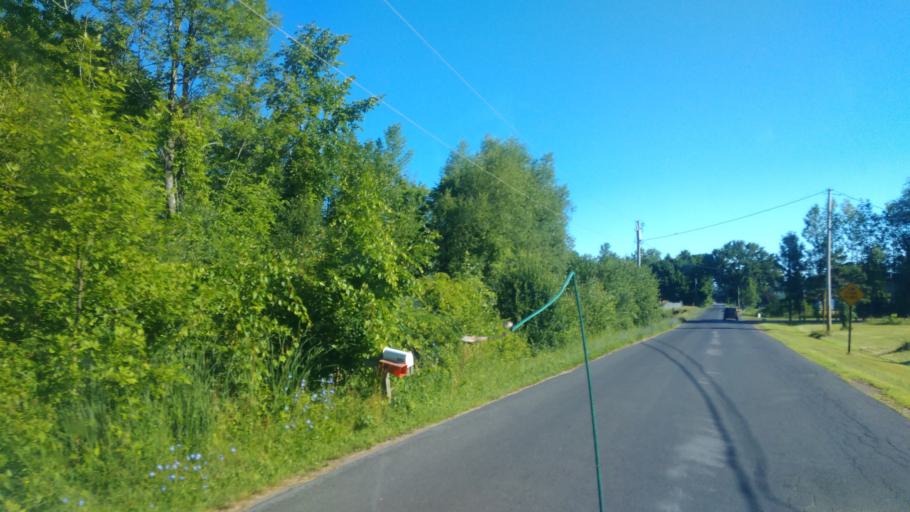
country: US
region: New York
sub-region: Wayne County
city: Sodus
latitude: 43.2333
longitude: -77.1110
